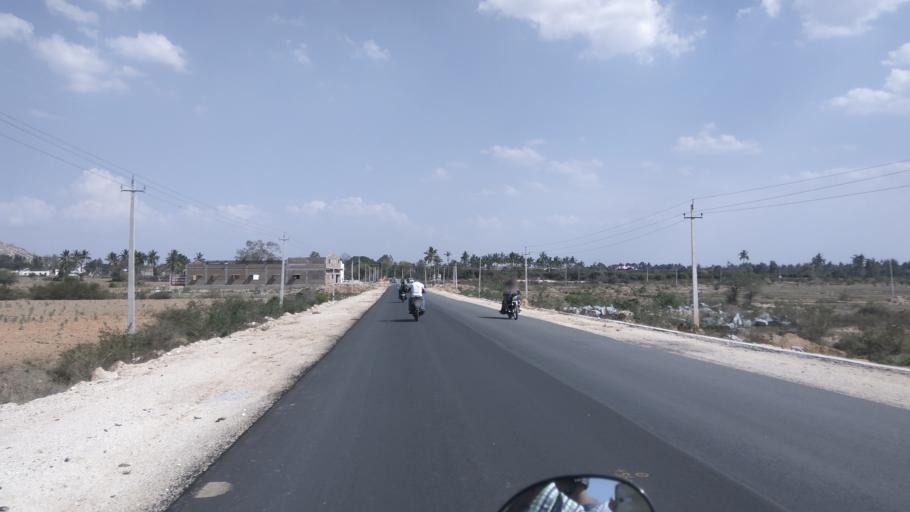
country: IN
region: Karnataka
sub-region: Kolar
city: Mulbagal
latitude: 13.1712
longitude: 78.3589
